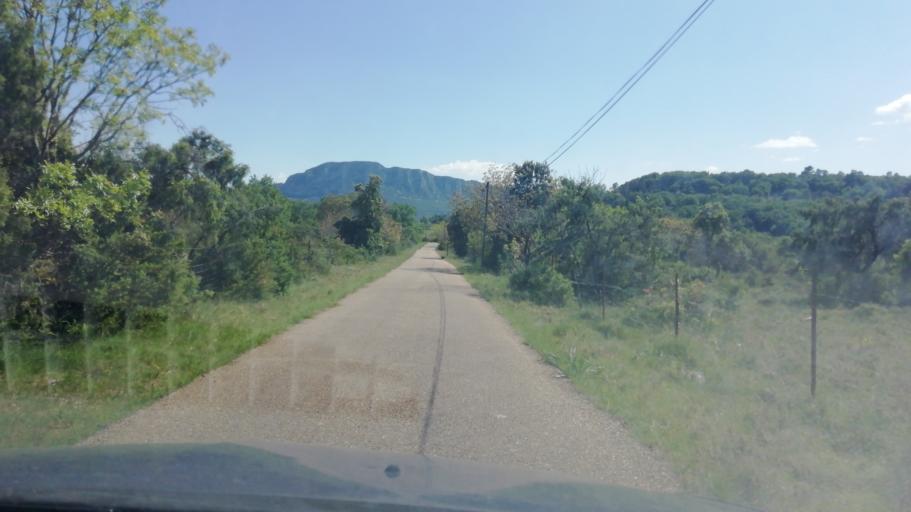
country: FR
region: Languedoc-Roussillon
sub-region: Departement de l'Herault
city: Saint-Mathieu-de-Treviers
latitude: 43.8240
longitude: 3.8118
